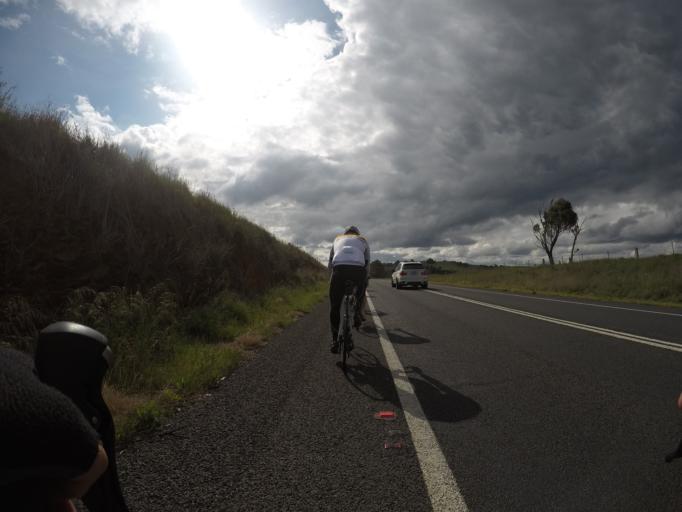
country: AU
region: New South Wales
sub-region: Blayney
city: Millthorpe
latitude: -33.3996
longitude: 149.2388
